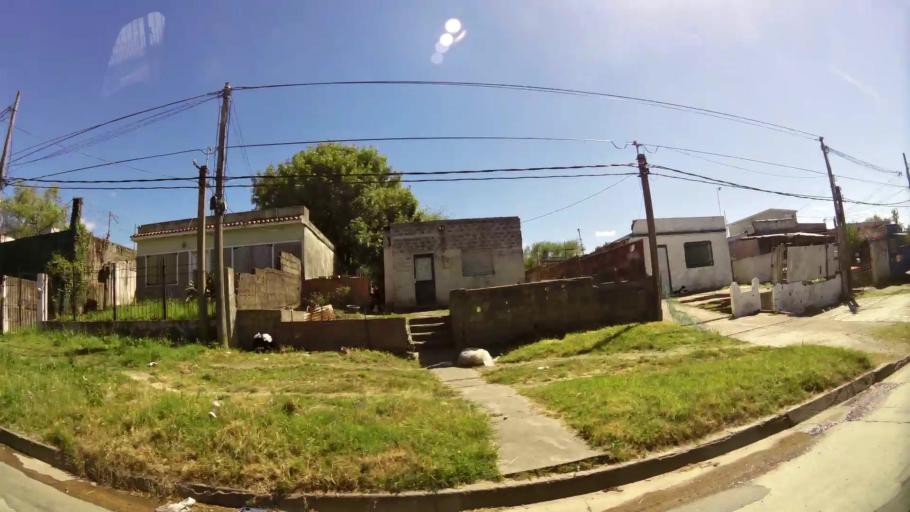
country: UY
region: Canelones
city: Paso de Carrasco
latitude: -34.8491
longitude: -56.1213
